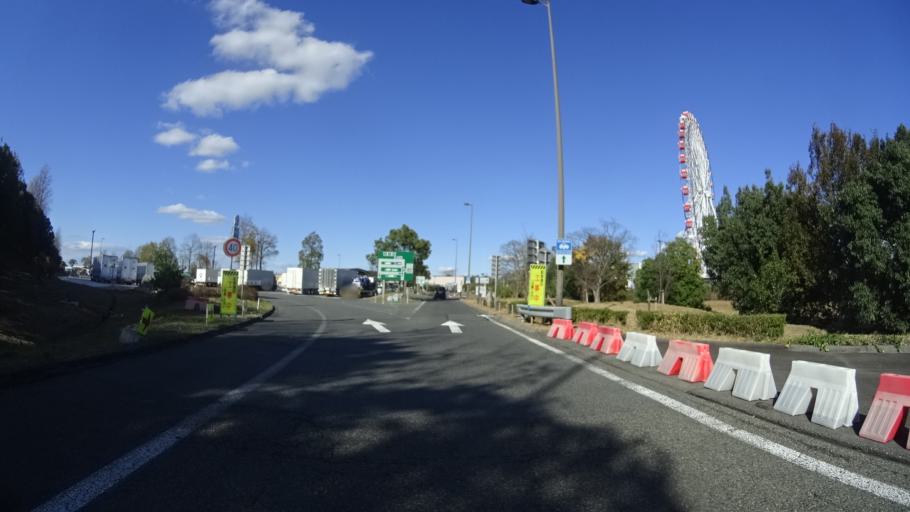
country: JP
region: Aichi
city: Chiryu
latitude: 35.0397
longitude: 137.0476
